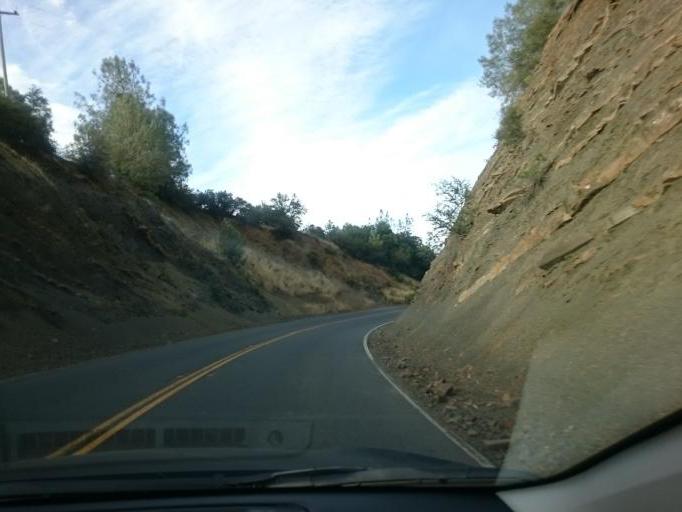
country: US
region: California
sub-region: Yolo County
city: Winters
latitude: 38.4670
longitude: -122.1524
